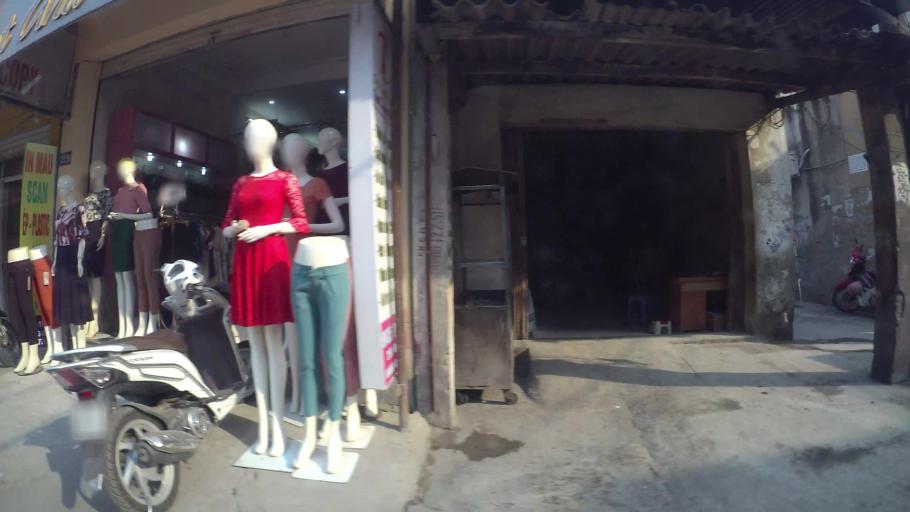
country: VN
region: Ha Noi
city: Hai BaTrung
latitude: 20.9824
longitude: 105.8334
